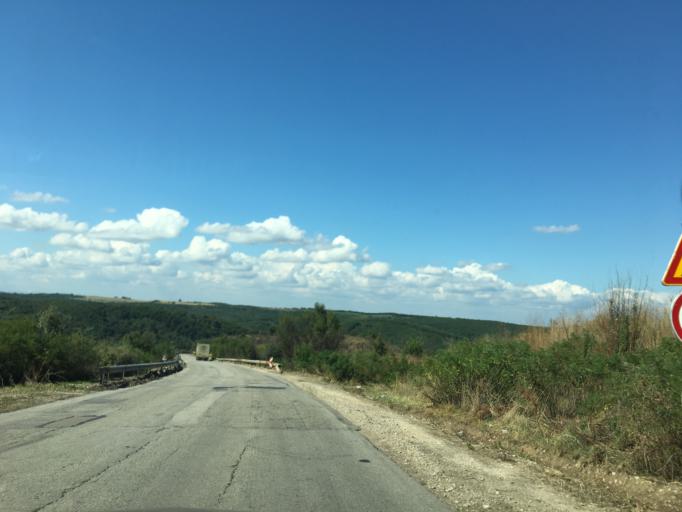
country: RO
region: Dolj
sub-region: Comuna Desa
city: Desa
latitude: 43.7590
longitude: 23.0021
